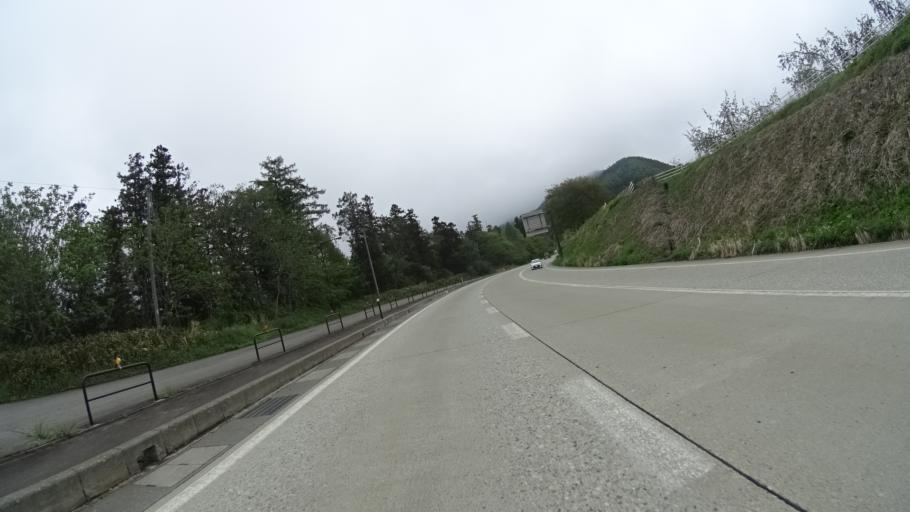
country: JP
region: Nagano
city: Nakano
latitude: 36.7341
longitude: 138.4191
